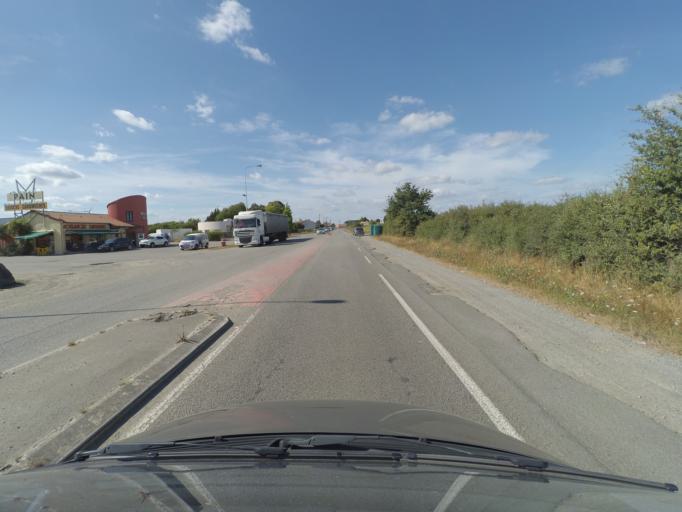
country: FR
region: Pays de la Loire
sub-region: Departement de la Loire-Atlantique
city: Les Sorinieres
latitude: 47.1132
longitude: -1.5401
